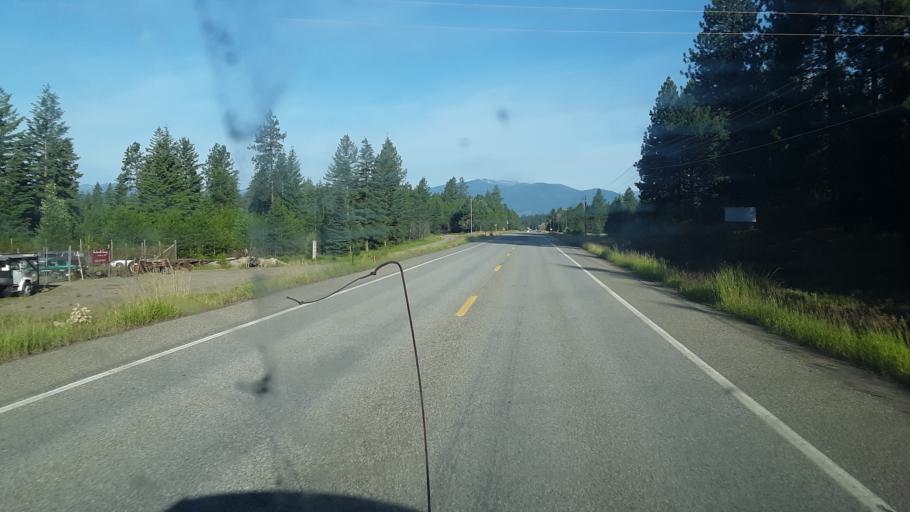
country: US
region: Idaho
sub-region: Boundary County
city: Bonners Ferry
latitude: 48.7280
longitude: -116.2211
